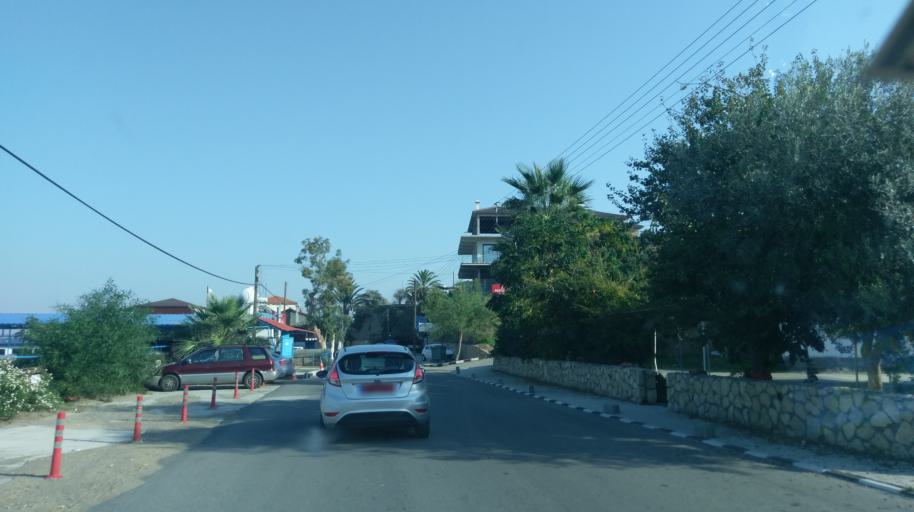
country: CY
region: Lefkosia
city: Lefka
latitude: 35.1490
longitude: 32.8004
